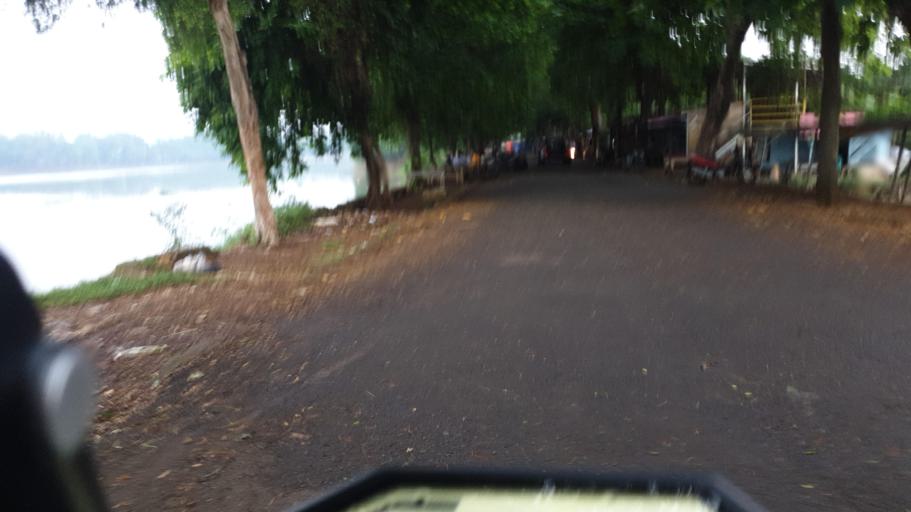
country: ID
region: West Java
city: Depok
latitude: -6.3444
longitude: 106.8223
